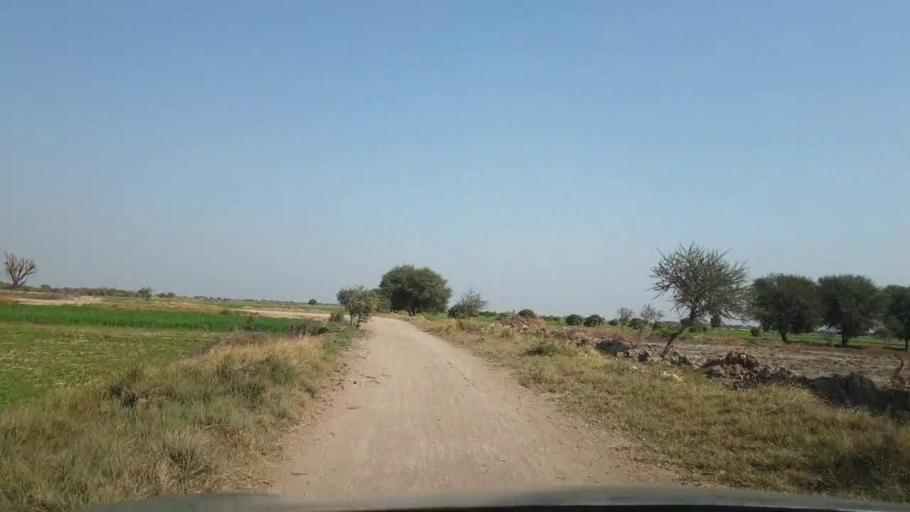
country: PK
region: Sindh
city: Berani
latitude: 25.6209
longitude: 68.8314
